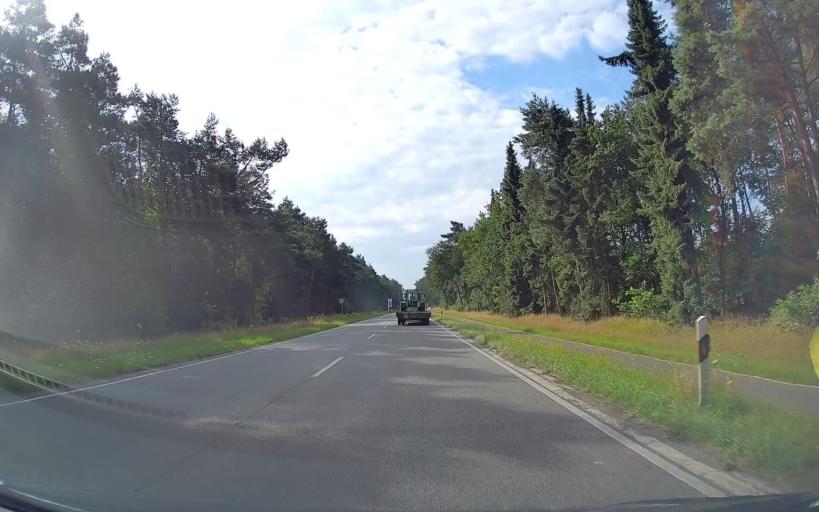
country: DE
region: Lower Saxony
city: Bosel
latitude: 52.9666
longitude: 7.9195
